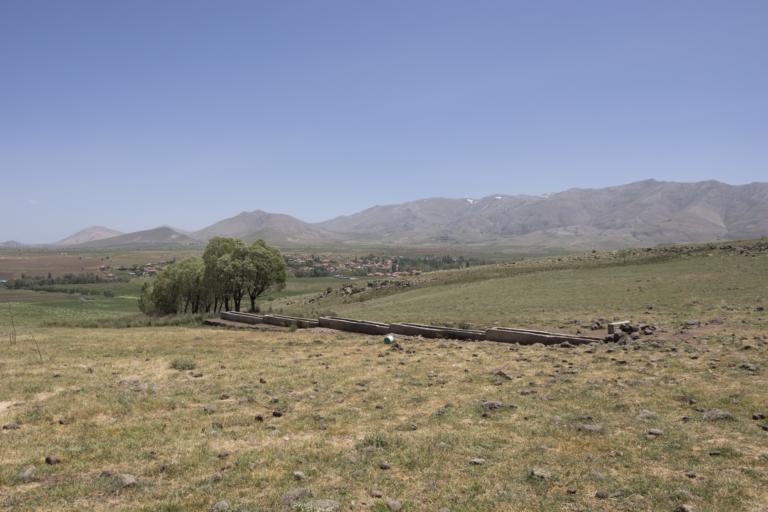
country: TR
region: Kayseri
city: Toklar
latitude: 38.4609
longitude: 36.0616
